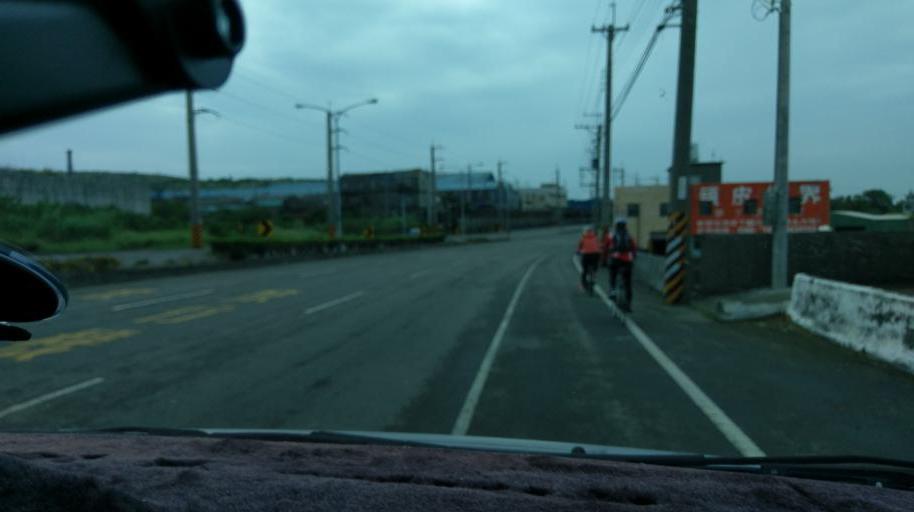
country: TW
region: Taiwan
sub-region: Miaoli
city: Miaoli
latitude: 24.4781
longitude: 120.6740
